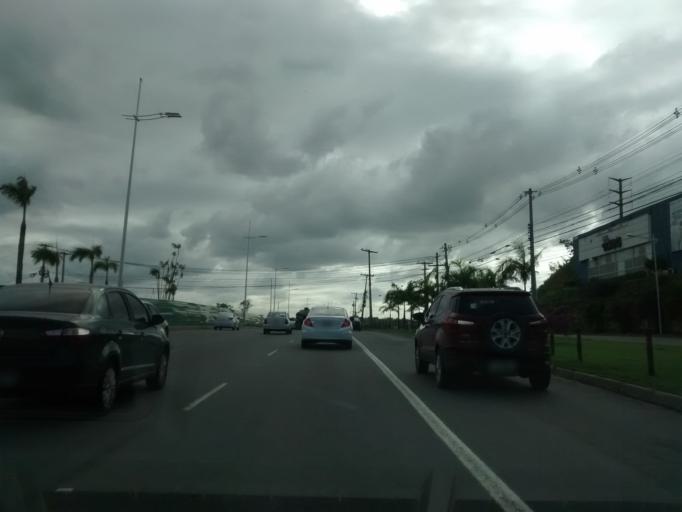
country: BR
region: Bahia
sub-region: Lauro De Freitas
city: Lauro de Freitas
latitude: -12.9292
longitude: -38.3873
